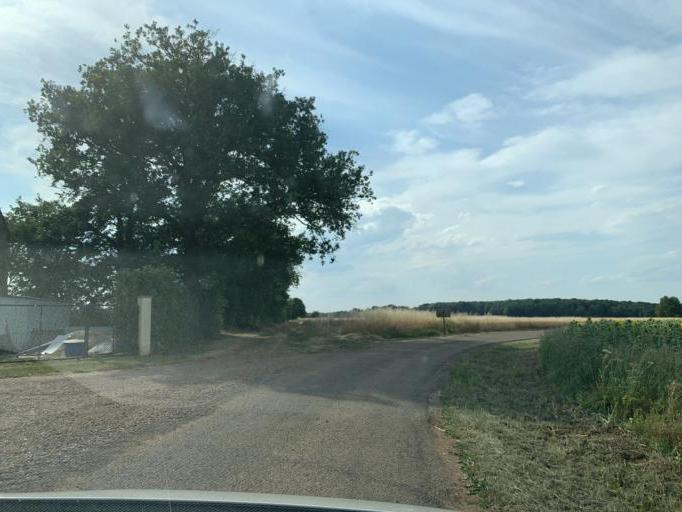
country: FR
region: Bourgogne
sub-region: Departement de l'Yonne
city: Fontenailles
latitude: 47.4992
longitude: 3.4293
